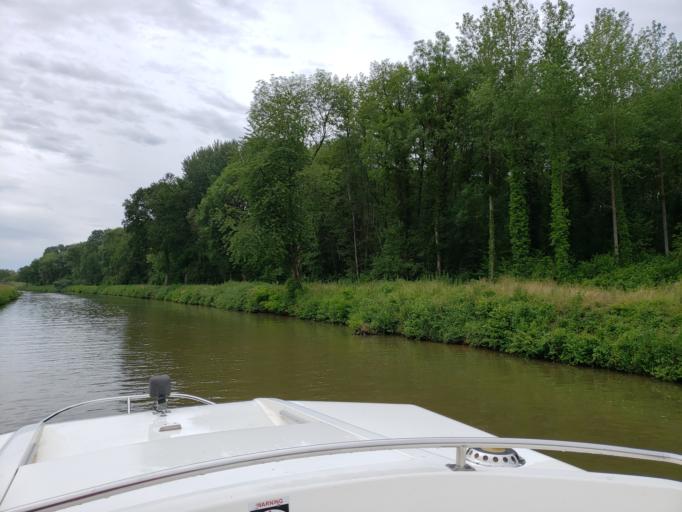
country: FR
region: Bourgogne
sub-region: Departement de l'Yonne
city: Appoigny
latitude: 47.9015
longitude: 3.5350
